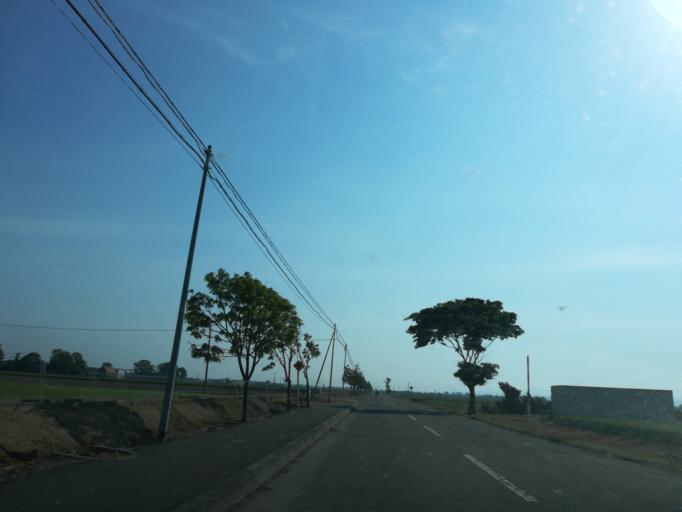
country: JP
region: Hokkaido
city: Iwamizawa
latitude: 43.1558
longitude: 141.6765
